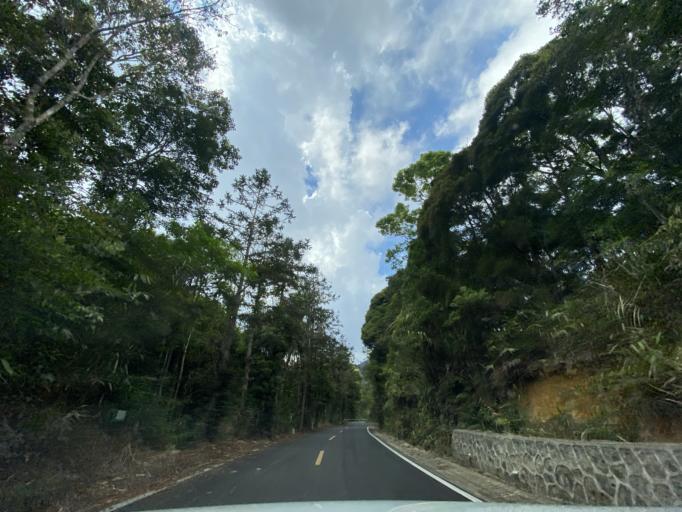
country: CN
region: Hainan
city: Diaoluoshan
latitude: 18.7215
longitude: 109.8708
